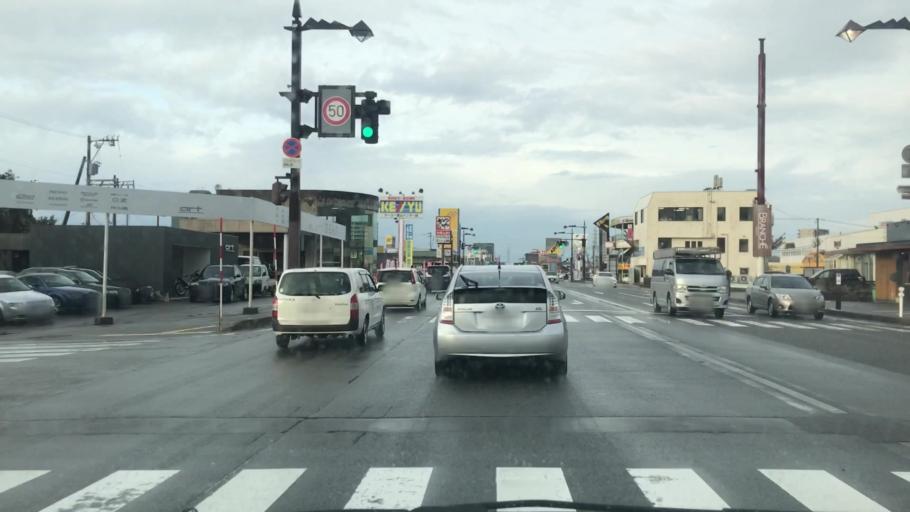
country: JP
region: Toyama
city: Toyama-shi
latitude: 36.6591
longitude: 137.2098
